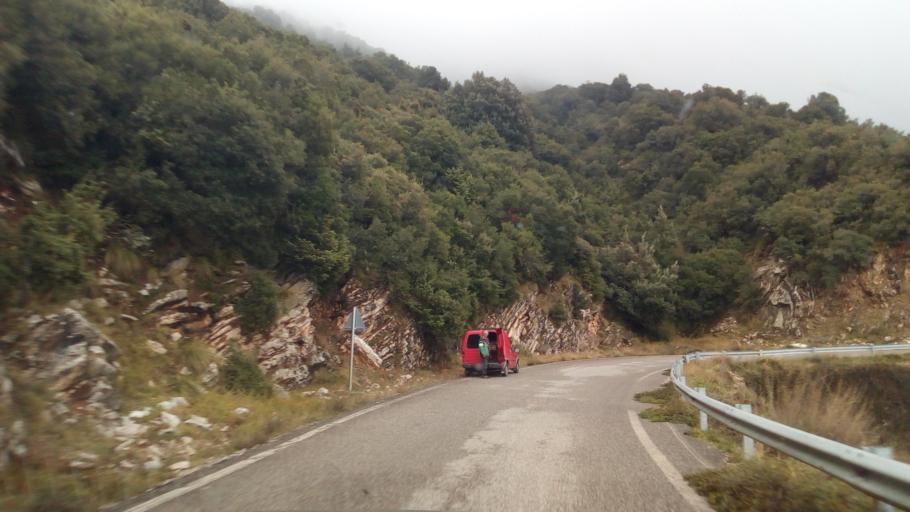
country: GR
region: West Greece
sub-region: Nomos Aitolias kai Akarnanias
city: Nafpaktos
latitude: 38.5142
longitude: 21.8419
